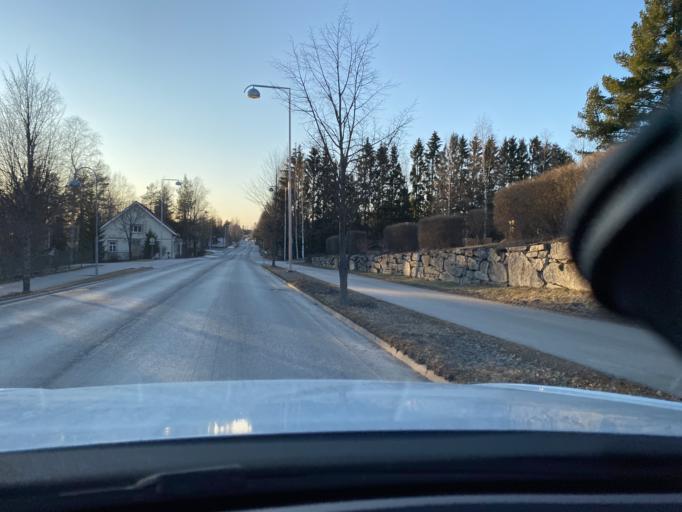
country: FI
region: Pirkanmaa
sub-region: Lounais-Pirkanmaa
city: Punkalaidun
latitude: 61.1146
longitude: 23.0959
